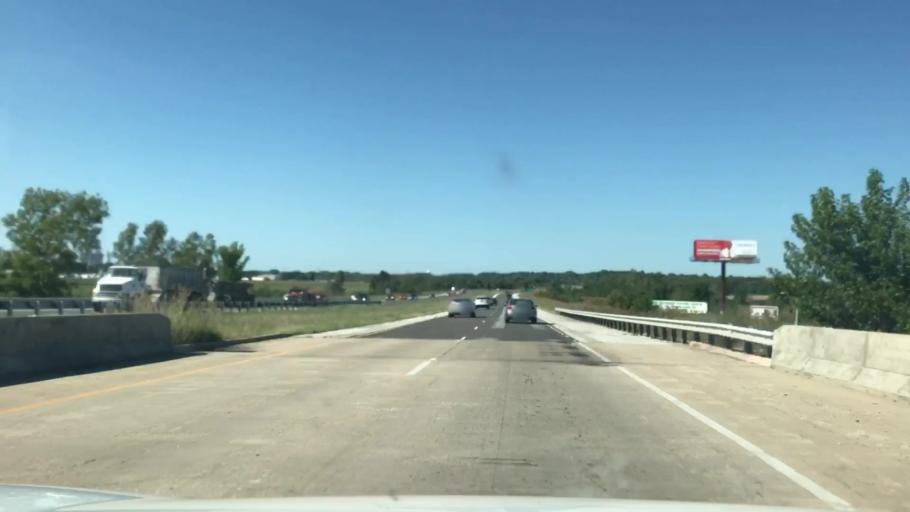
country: US
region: Illinois
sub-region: Madison County
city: South Roxana
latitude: 38.8203
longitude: -90.0423
